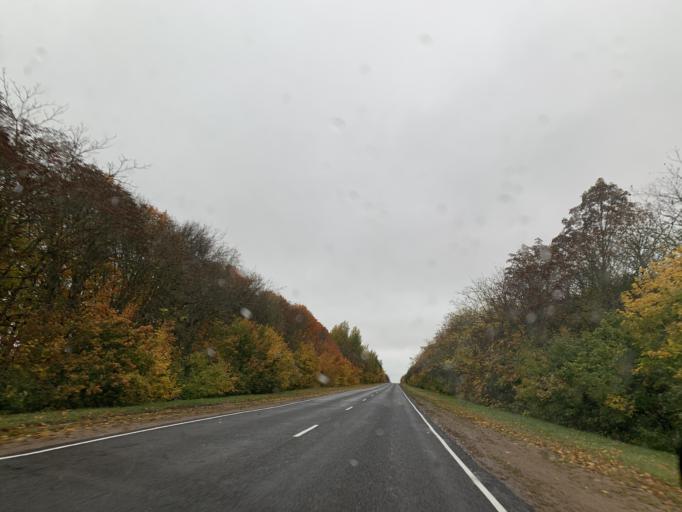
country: BY
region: Minsk
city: Haradzyeya
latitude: 53.3867
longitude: 26.5676
